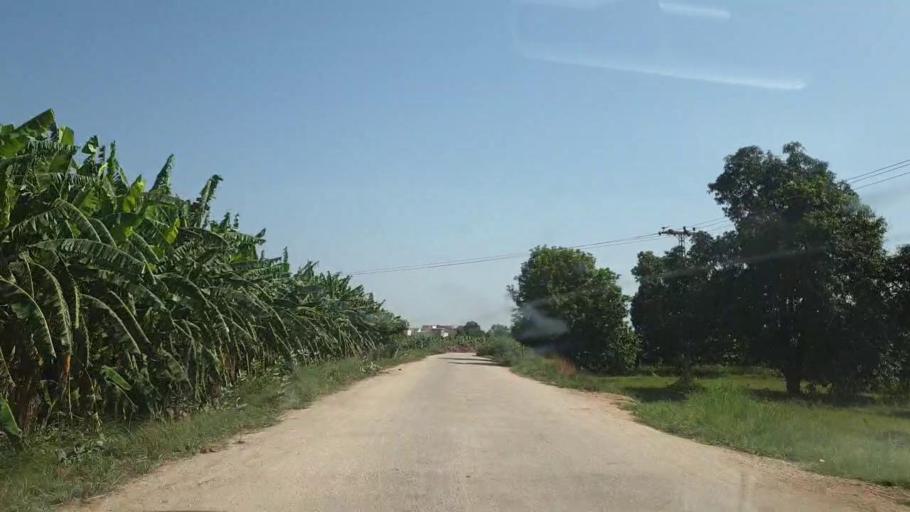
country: PK
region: Sindh
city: Tando Jam
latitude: 25.4026
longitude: 68.5853
